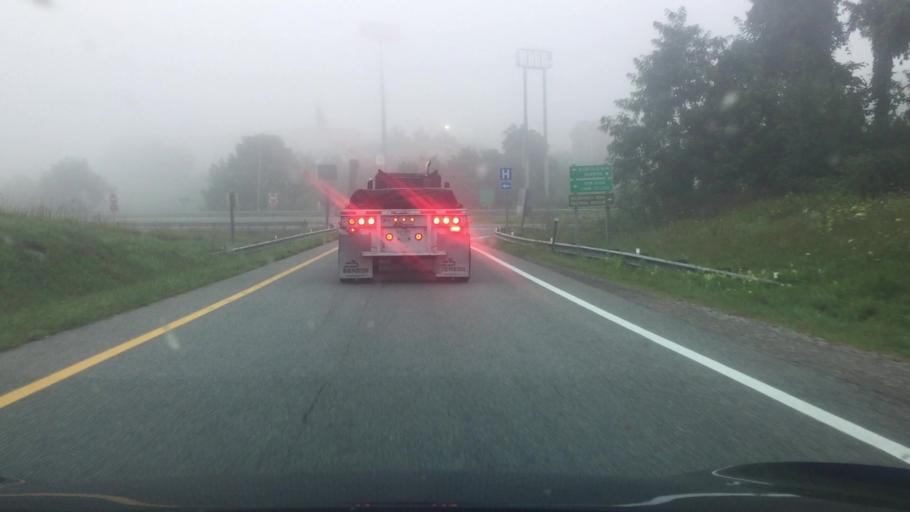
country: US
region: Virginia
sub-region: Pulaski County
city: Dublin
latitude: 37.0762
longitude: -80.6944
